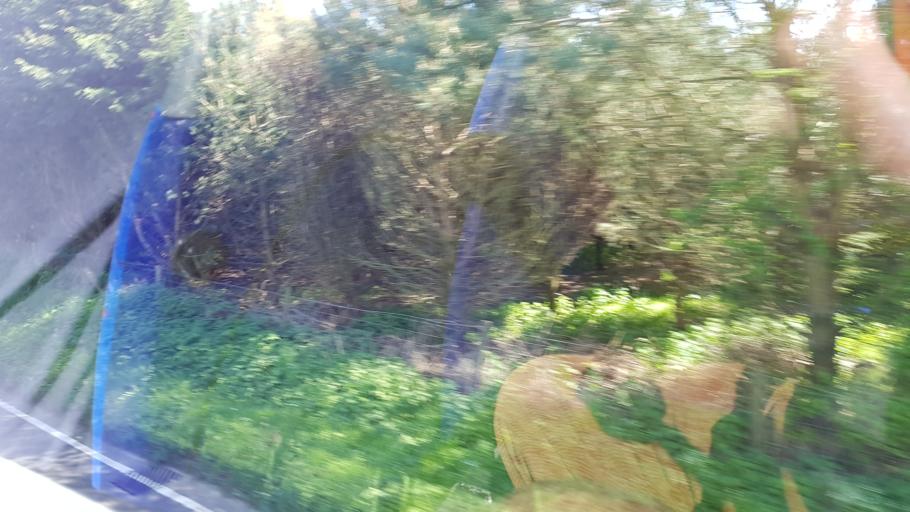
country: GB
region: England
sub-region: Isle of Wight
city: Newchurch
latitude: 50.6499
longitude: -1.2146
